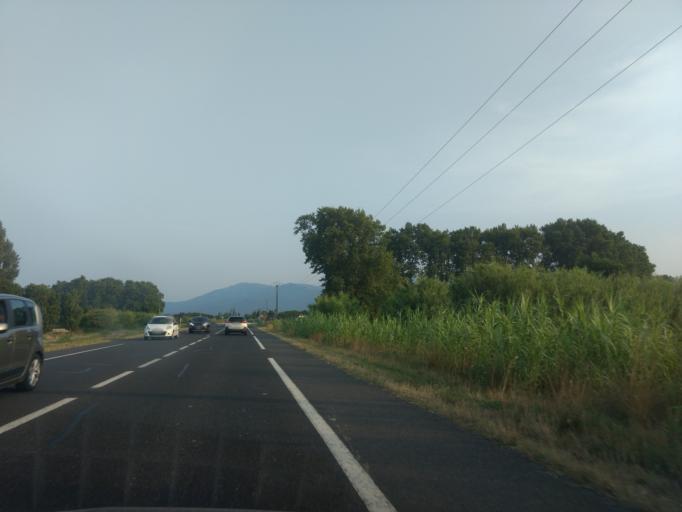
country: FR
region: Languedoc-Roussillon
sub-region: Departement des Pyrenees-Orientales
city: Latour-Bas-Elne
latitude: 42.5985
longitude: 3.0246
